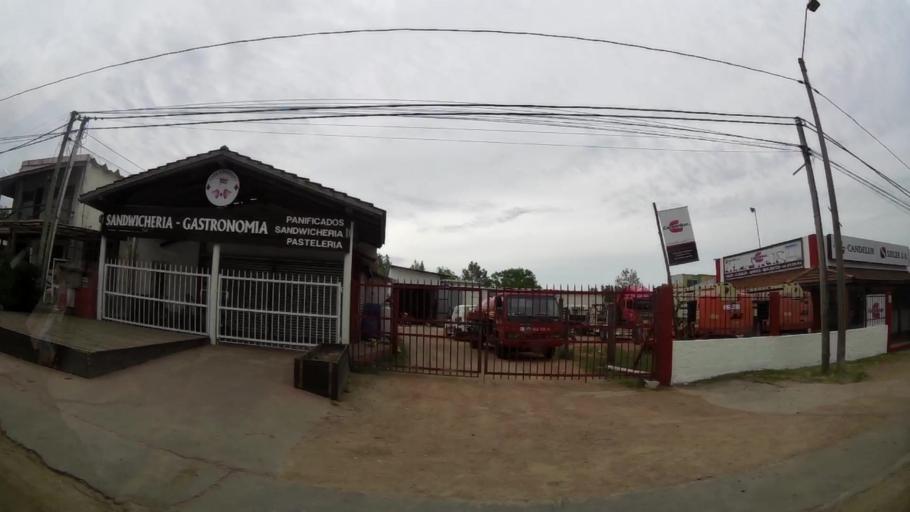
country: UY
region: Maldonado
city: Maldonado
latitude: -34.9140
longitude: -54.9424
